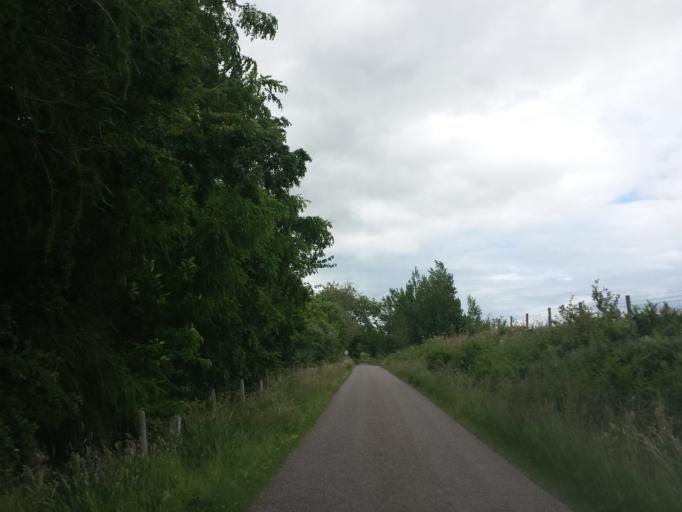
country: GB
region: Scotland
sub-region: Highland
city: Fortrose
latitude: 57.5109
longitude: -4.0398
